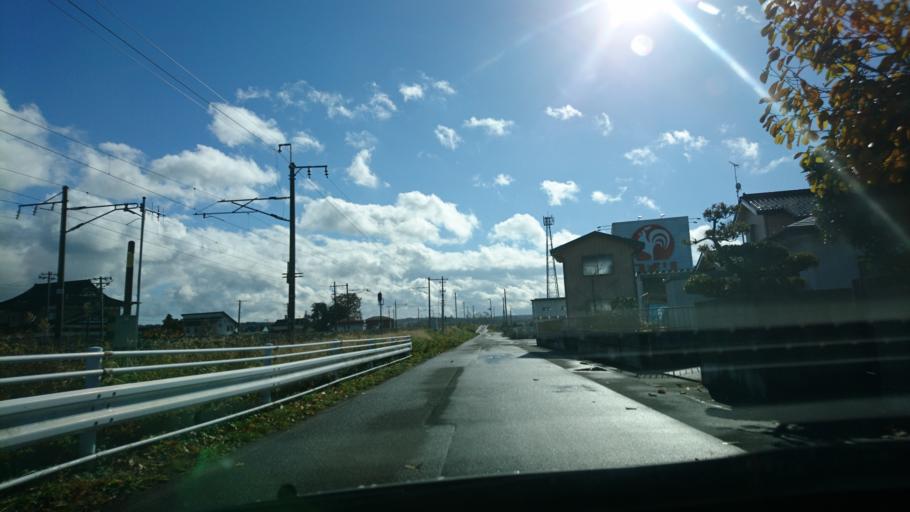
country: JP
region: Iwate
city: Ichinoseki
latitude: 38.9402
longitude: 141.1361
